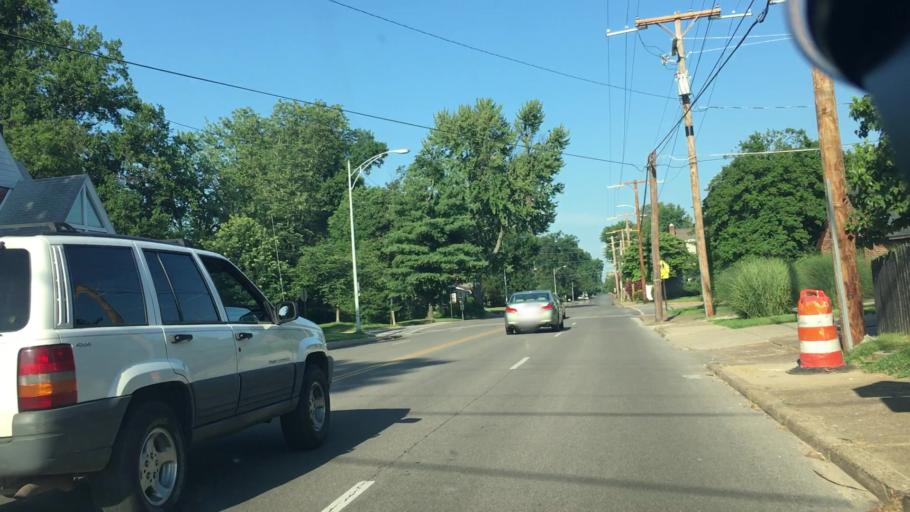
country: US
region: Indiana
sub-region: Vanderburgh County
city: Evansville
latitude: 37.9735
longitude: -87.5255
